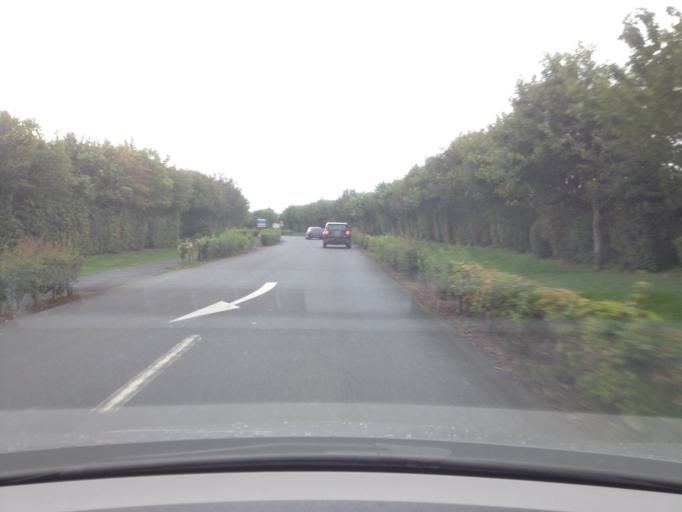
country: FR
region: Lower Normandy
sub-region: Departement du Calvados
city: Grandcamp-Maisy
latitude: 49.3905
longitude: -0.9907
